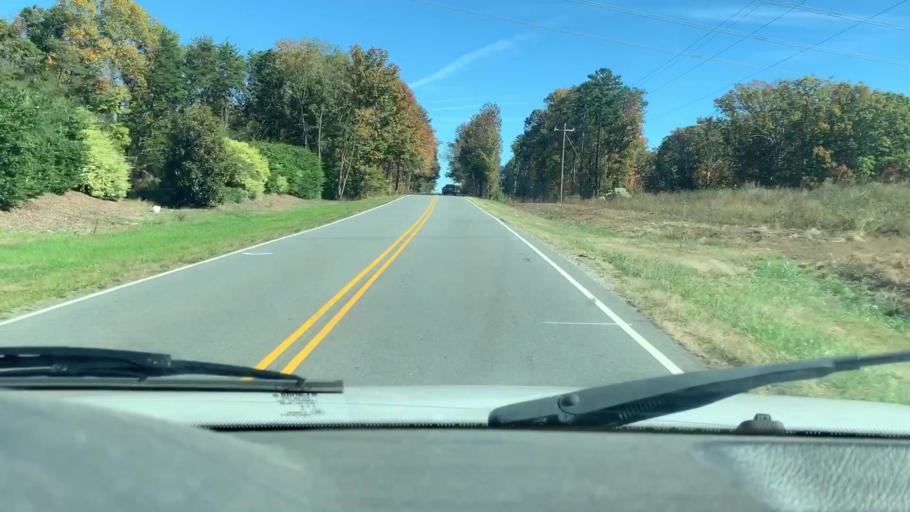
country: US
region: North Carolina
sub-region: Lincoln County
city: Lowesville
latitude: 35.4269
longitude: -80.9471
